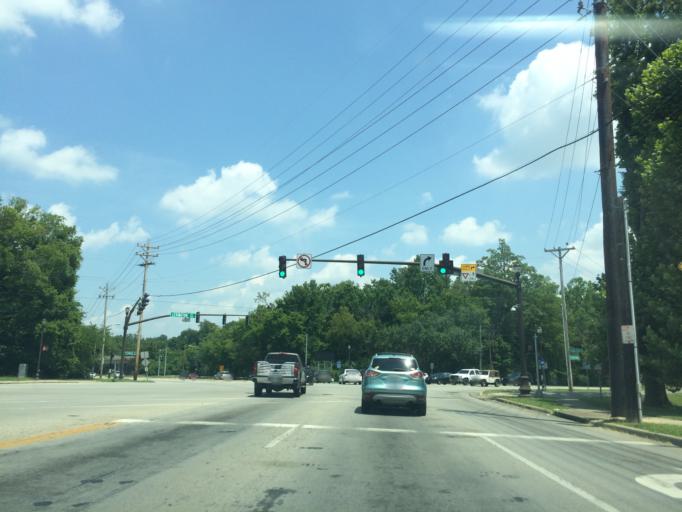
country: US
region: Kentucky
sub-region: Jefferson County
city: Saint Matthews
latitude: 38.2452
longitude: -85.7020
